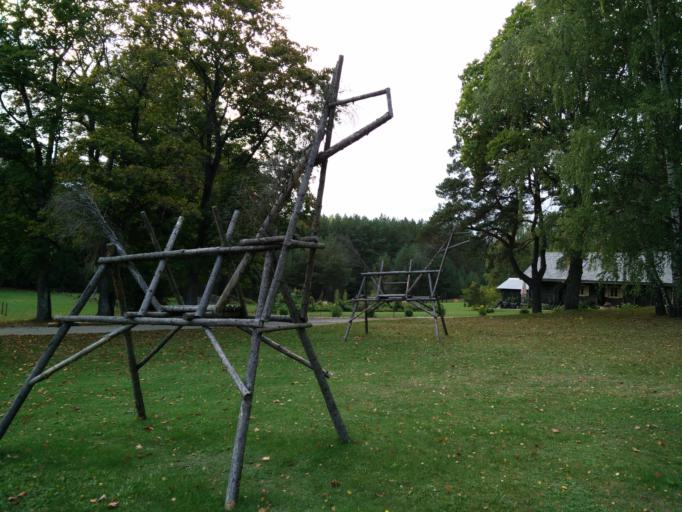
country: LT
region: Utenos apskritis
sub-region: Anyksciai
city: Anyksciai
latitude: 55.5730
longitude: 25.0858
